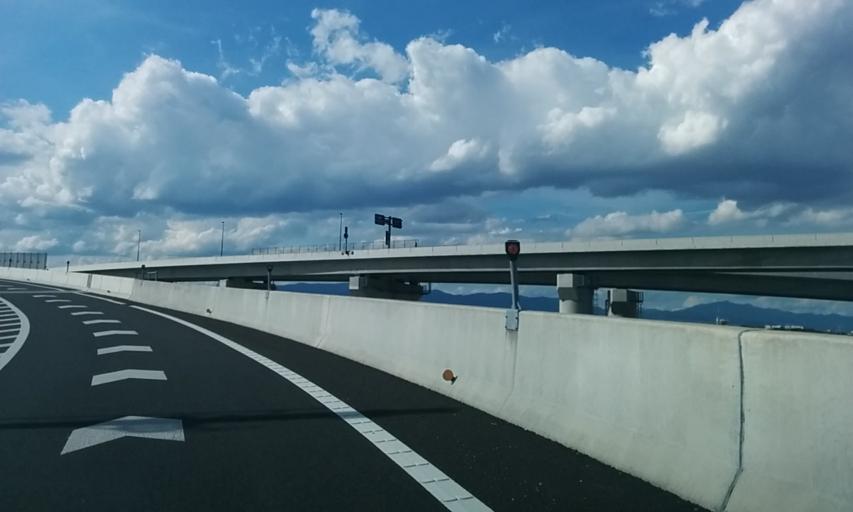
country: JP
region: Kyoto
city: Tanabe
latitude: 34.8460
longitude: 135.7610
